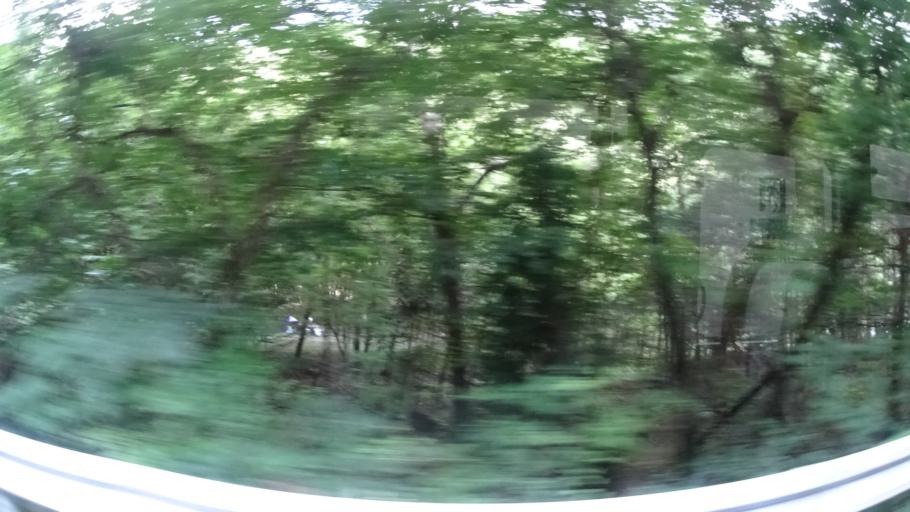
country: JP
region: Tochigi
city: Nikko
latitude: 36.6928
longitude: 139.5008
